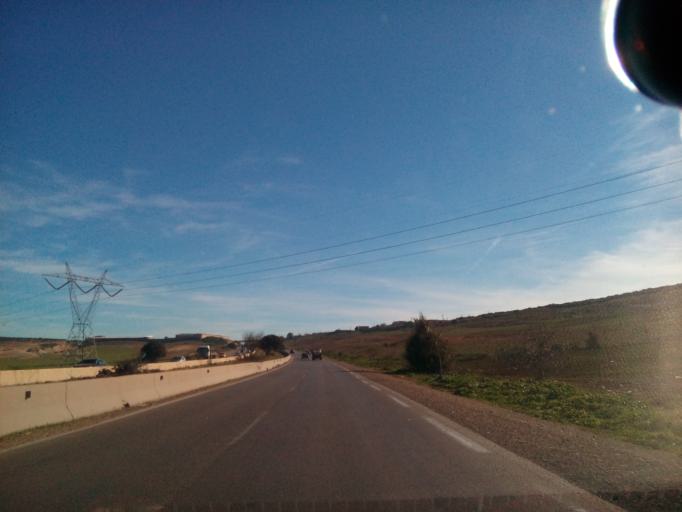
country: DZ
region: Oran
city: Ain el Bya
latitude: 35.7680
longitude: -0.2312
